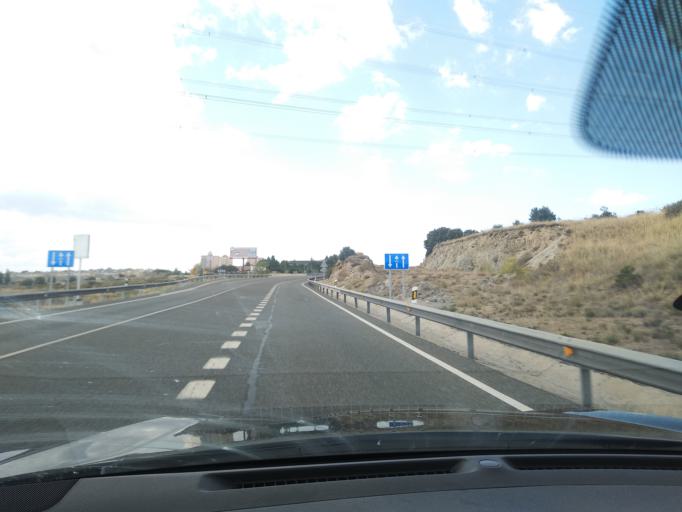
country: ES
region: Castille and Leon
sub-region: Provincia de Segovia
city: Otero de Herreros
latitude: 40.7734
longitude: -4.2032
